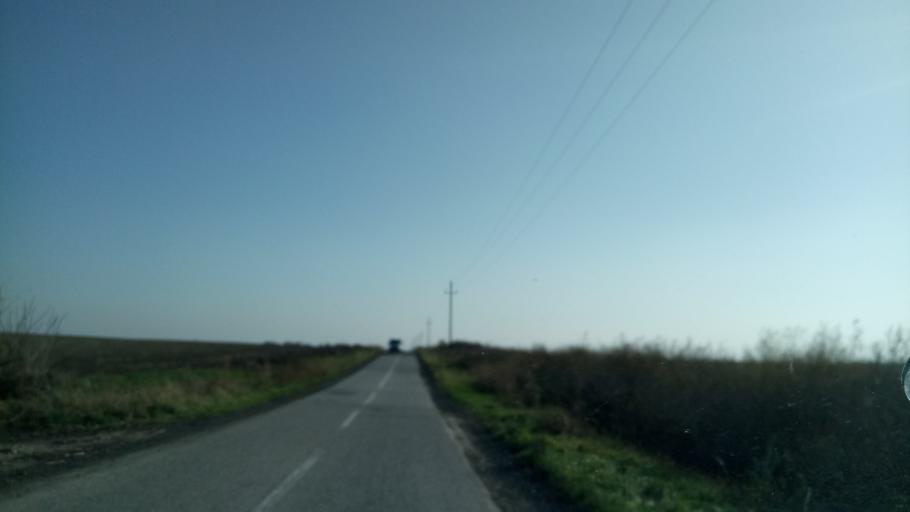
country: RS
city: Ljukovo
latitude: 45.0380
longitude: 20.0401
